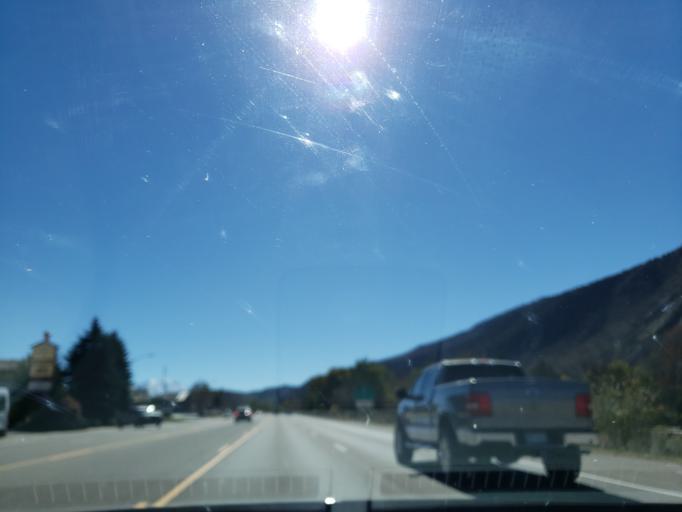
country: US
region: Colorado
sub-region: Garfield County
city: Glenwood Springs
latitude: 39.5240
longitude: -107.3221
